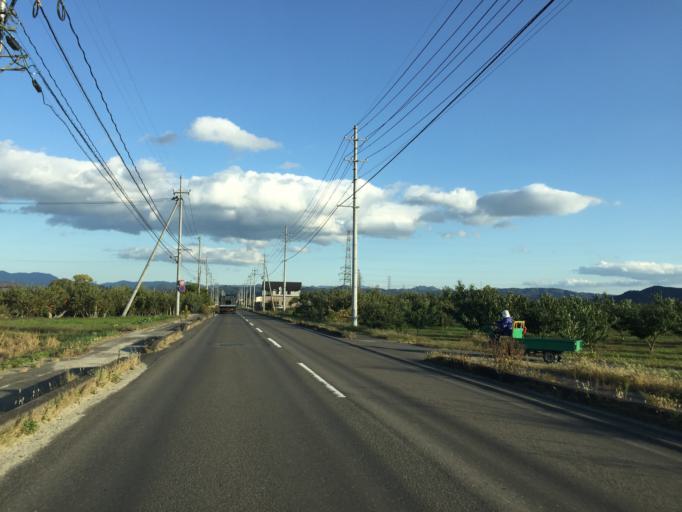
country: JP
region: Fukushima
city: Fukushima-shi
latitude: 37.8177
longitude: 140.4550
